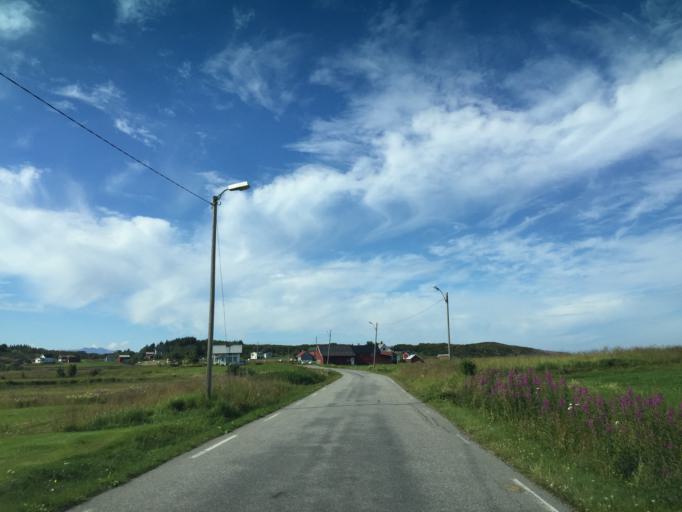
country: NO
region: Nordland
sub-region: Vagan
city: Kabelvag
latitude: 68.3932
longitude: 14.4624
